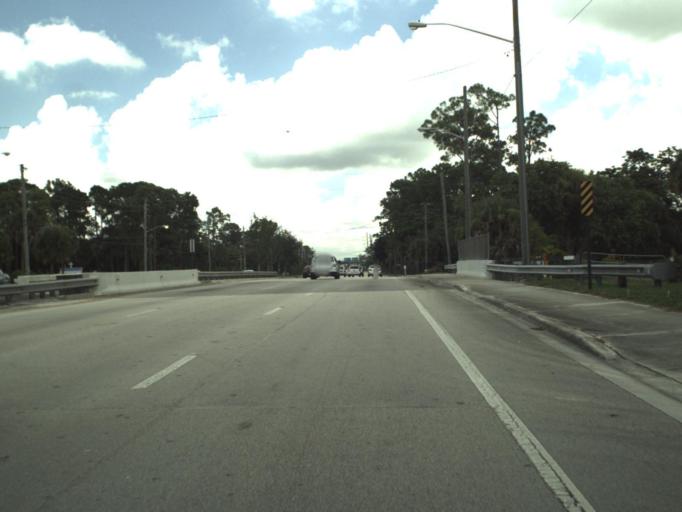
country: US
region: Florida
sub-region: Palm Beach County
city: Lake Belvedere Estates
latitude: 26.6698
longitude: -80.1450
